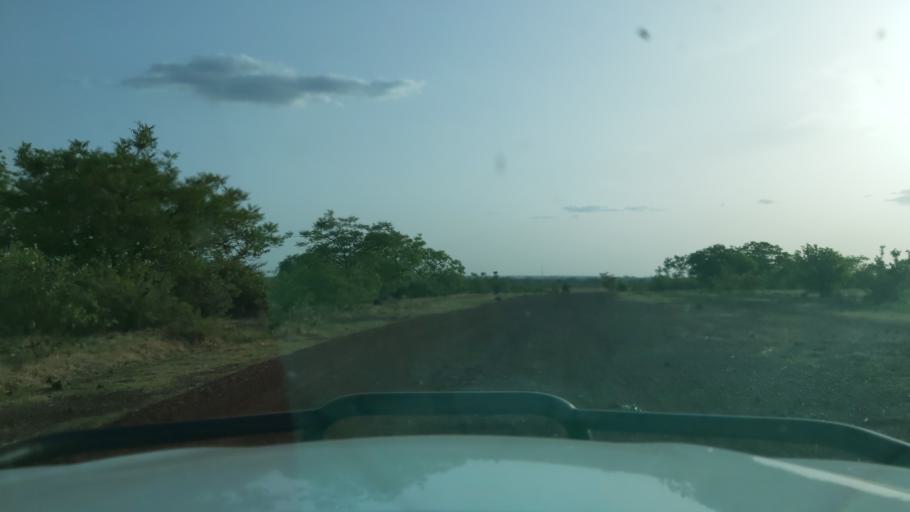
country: ML
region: Koulikoro
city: Kolokani
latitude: 13.2089
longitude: -7.9071
